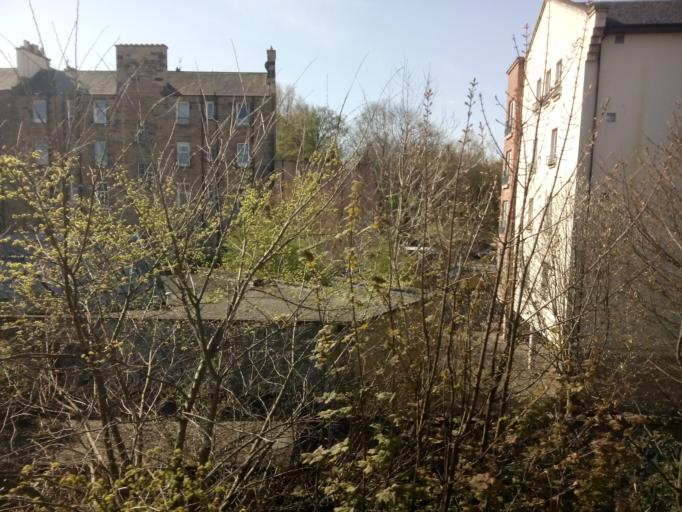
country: GB
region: Scotland
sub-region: West Lothian
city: Seafield
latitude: 55.9554
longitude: -3.1622
